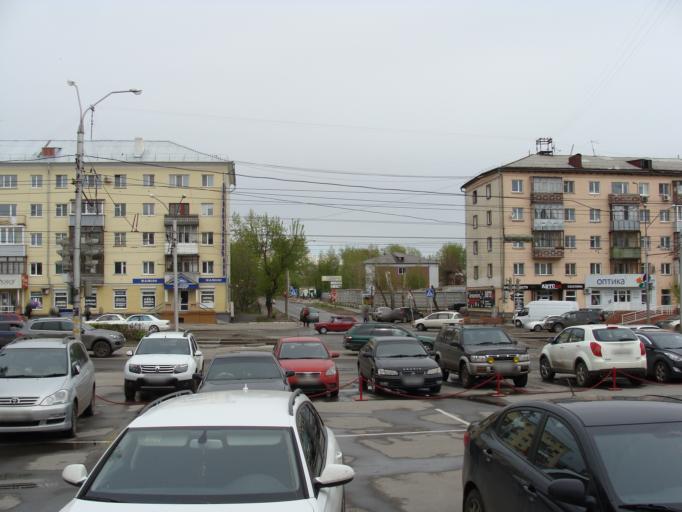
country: RU
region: Altai Krai
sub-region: Gorod Barnaulskiy
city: Barnaul
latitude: 53.3687
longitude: 83.7535
